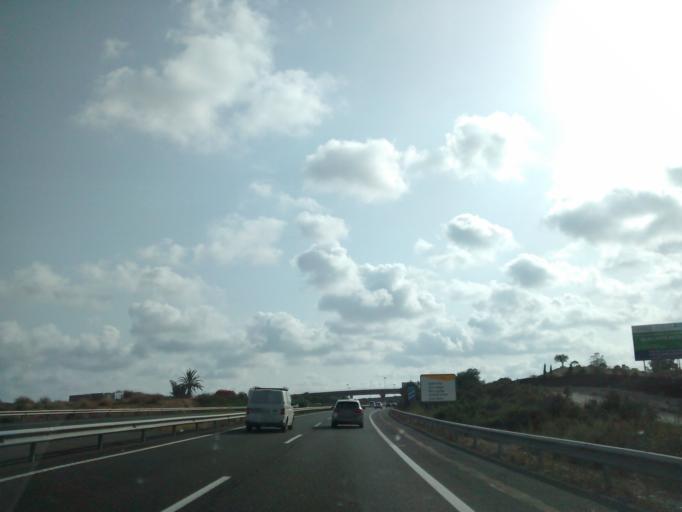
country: ES
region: Valencia
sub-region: Provincia de Alicante
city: el Campello
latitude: 38.4254
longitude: -0.4176
